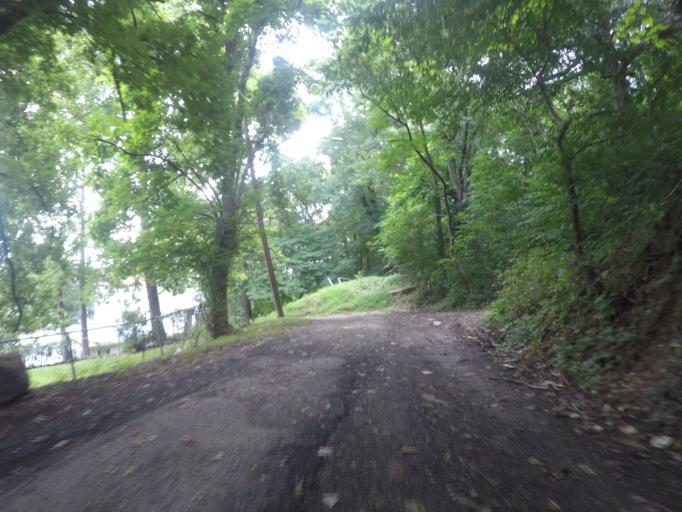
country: US
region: West Virginia
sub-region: Cabell County
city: Huntington
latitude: 38.4227
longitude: -82.3846
